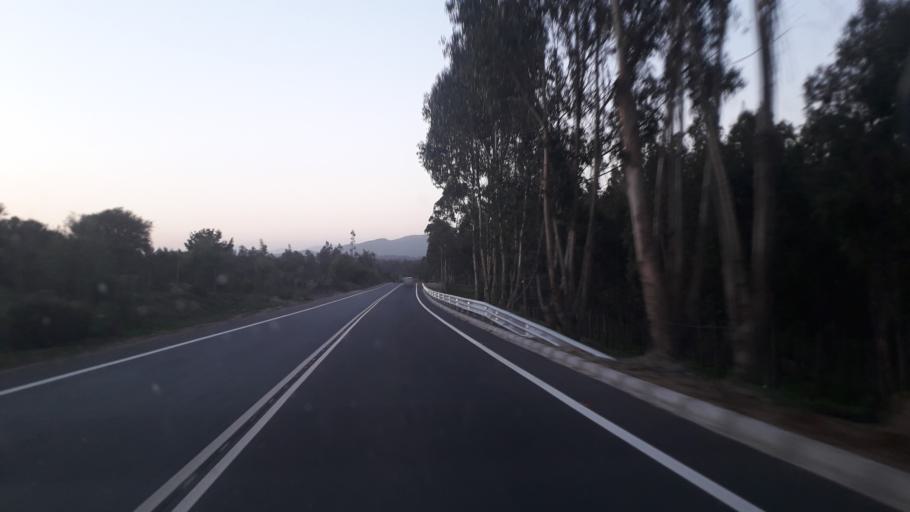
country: CL
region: Valparaiso
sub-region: Provincia de Quillota
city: Hacienda La Calera
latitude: -32.7506
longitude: -71.4190
